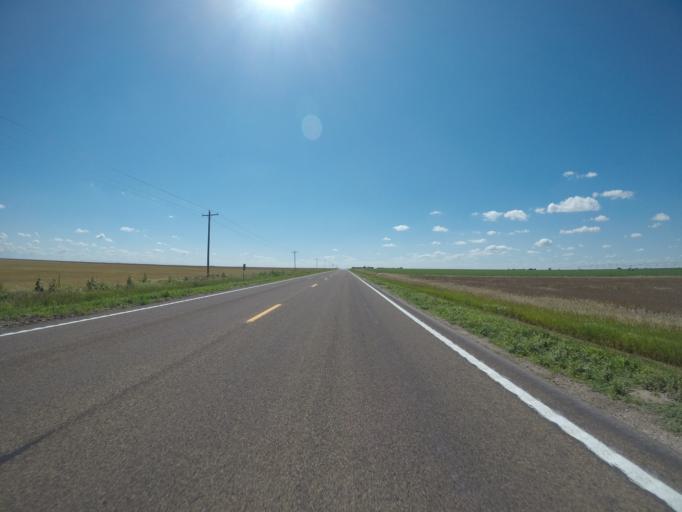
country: US
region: Nebraska
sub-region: Chase County
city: Imperial
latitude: 40.5376
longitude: -101.7468
